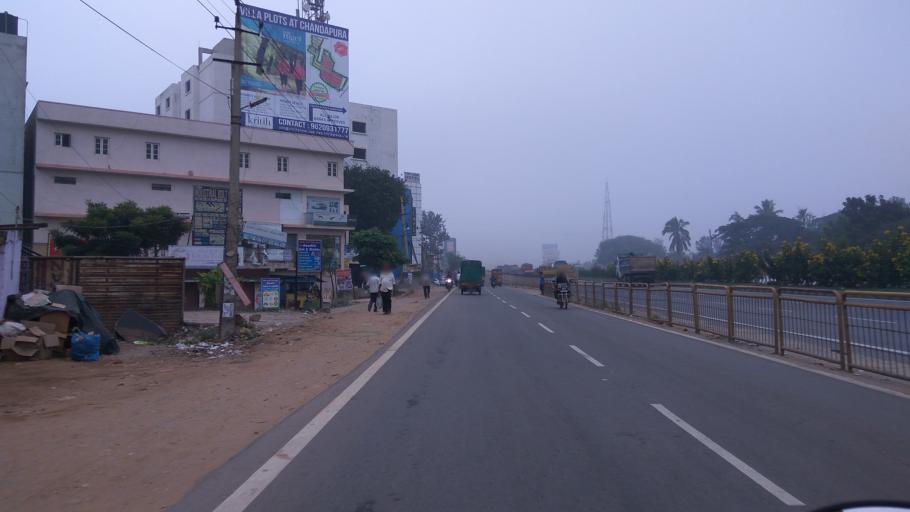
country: IN
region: Karnataka
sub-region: Bangalore Urban
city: Anekal
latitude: 12.8224
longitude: 77.6862
